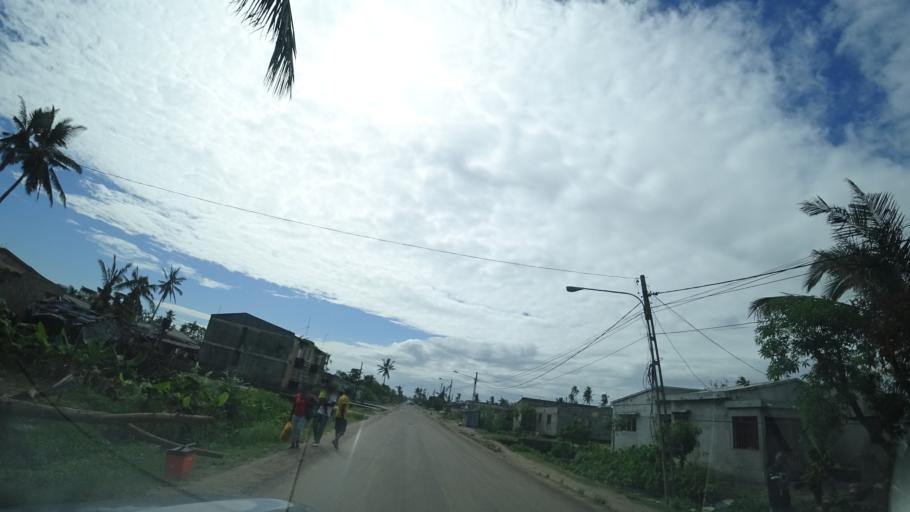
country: MZ
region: Sofala
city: Beira
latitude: -19.7660
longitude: 34.8672
